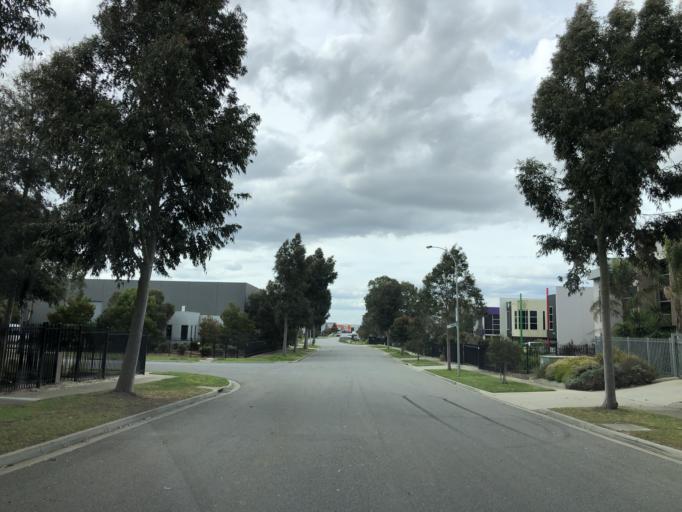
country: AU
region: Victoria
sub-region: Frankston
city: Carrum Downs
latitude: -38.0926
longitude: 145.1710
